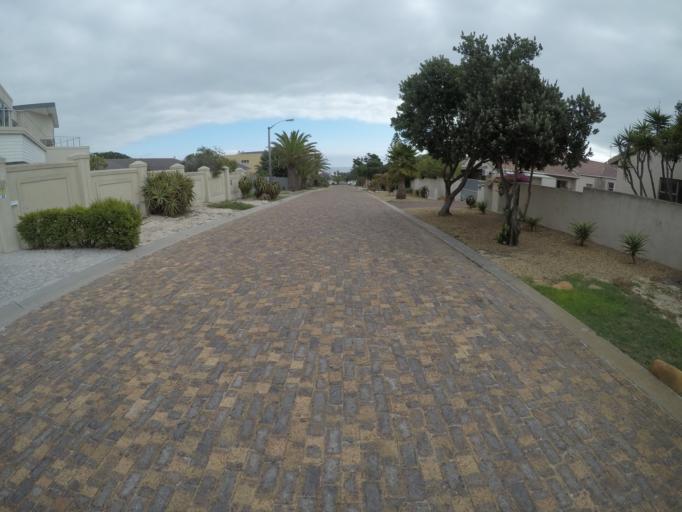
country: ZA
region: Western Cape
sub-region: City of Cape Town
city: Atlantis
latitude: -33.6927
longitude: 18.4411
